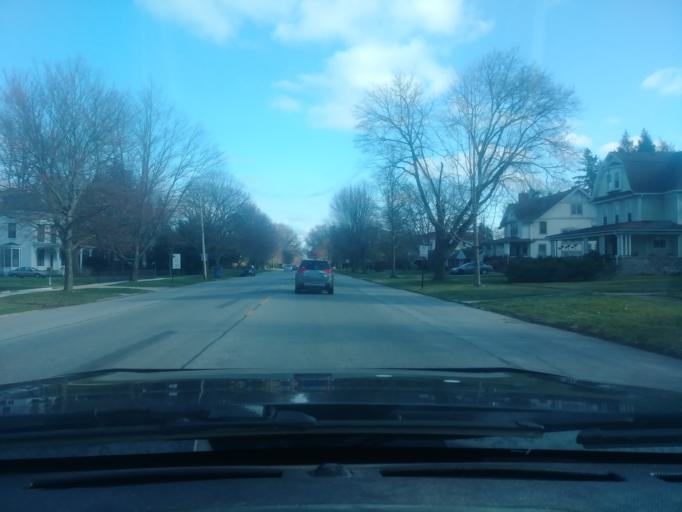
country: US
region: Indiana
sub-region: LaPorte County
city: LaPorte
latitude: 41.6037
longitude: -86.7161
